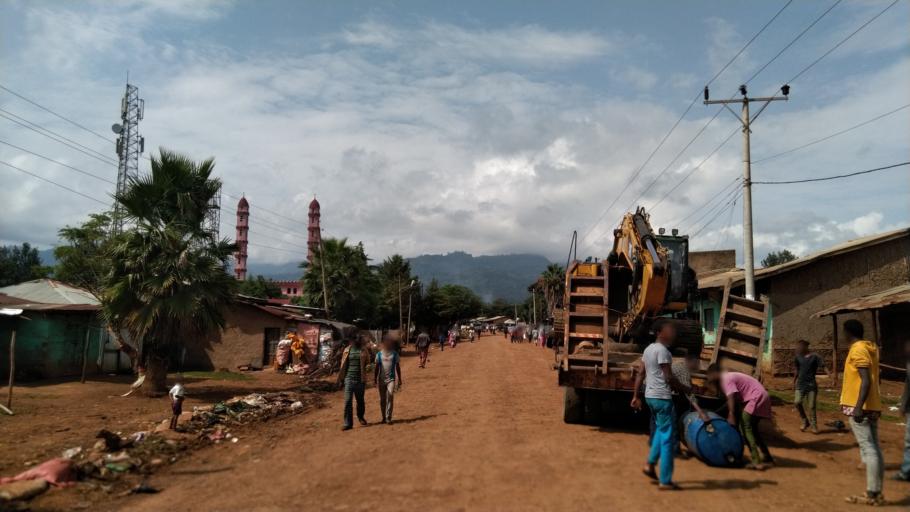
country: ET
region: Oromiya
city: Jima
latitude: 7.6342
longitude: 37.2521
